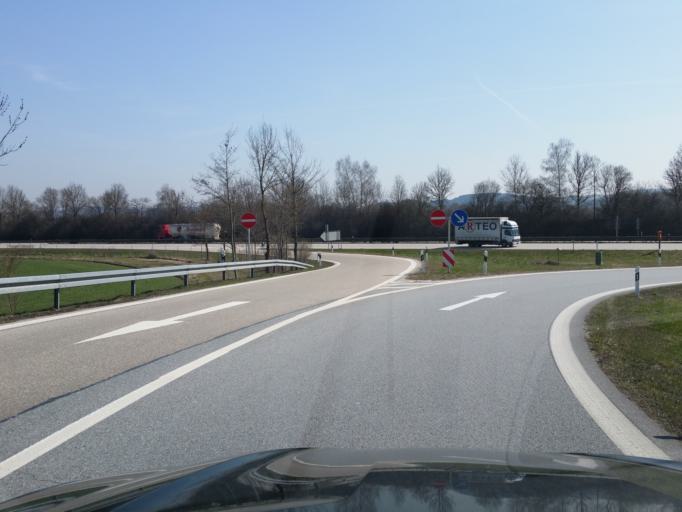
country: DE
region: Bavaria
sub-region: Upper Bavaria
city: Langenpreising
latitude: 48.4497
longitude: 11.9641
